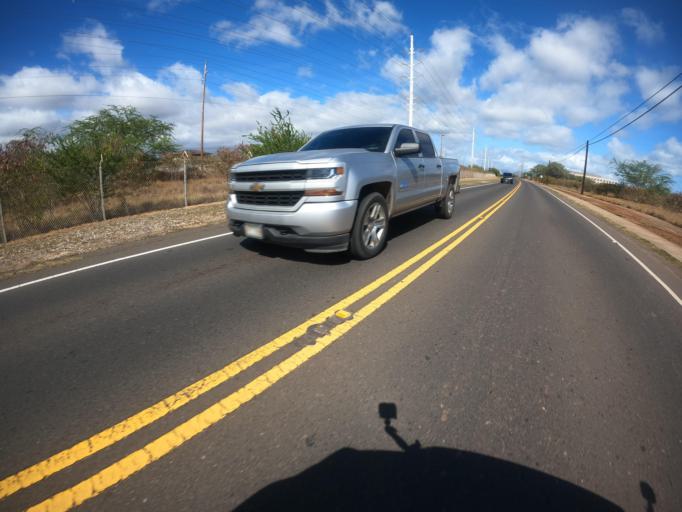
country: US
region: Hawaii
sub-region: Honolulu County
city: Makakilo City
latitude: 21.3233
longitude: -158.0724
